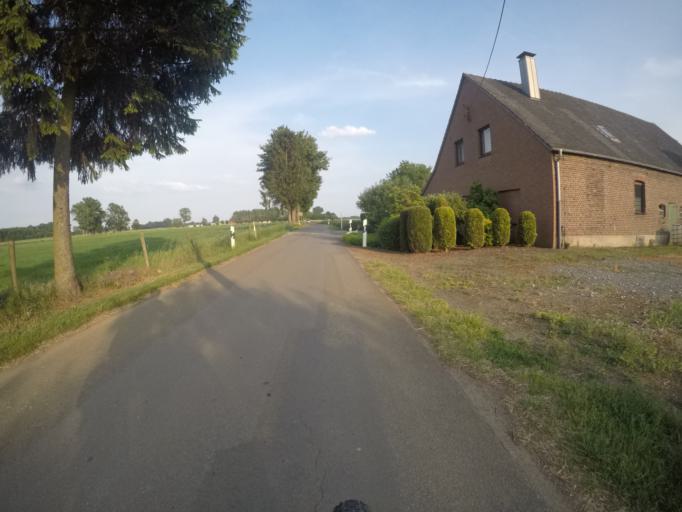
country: DE
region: North Rhine-Westphalia
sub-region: Regierungsbezirk Munster
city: Isselburg
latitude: 51.8281
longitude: 6.4732
